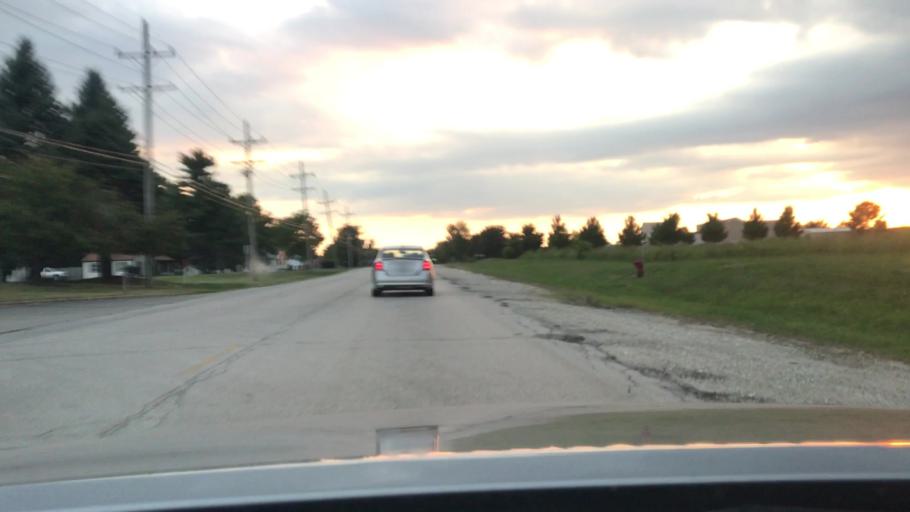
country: US
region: Illinois
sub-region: DuPage County
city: Warrenville
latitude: 41.7671
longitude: -88.2379
